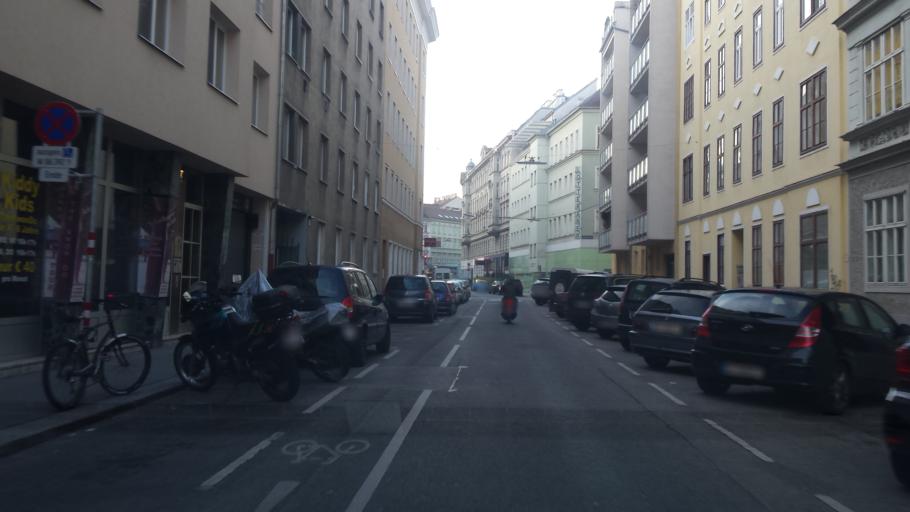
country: AT
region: Vienna
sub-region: Wien Stadt
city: Vienna
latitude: 48.2190
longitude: 16.3831
